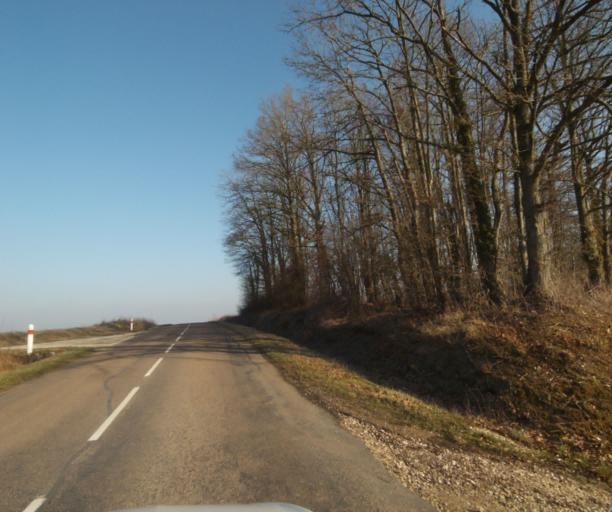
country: FR
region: Champagne-Ardenne
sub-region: Departement de la Haute-Marne
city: Montier-en-Der
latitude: 48.4313
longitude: 4.7523
